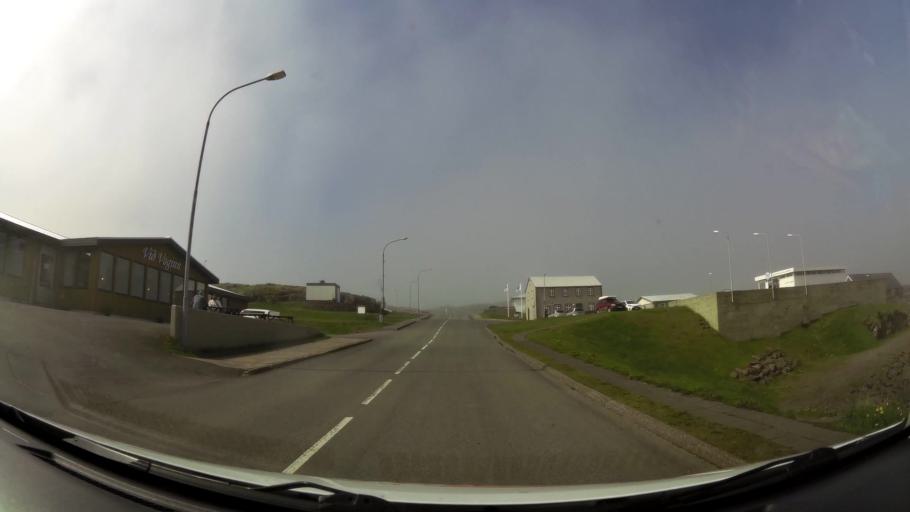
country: IS
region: East
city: Reydarfjoerdur
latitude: 64.6564
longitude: -14.2824
